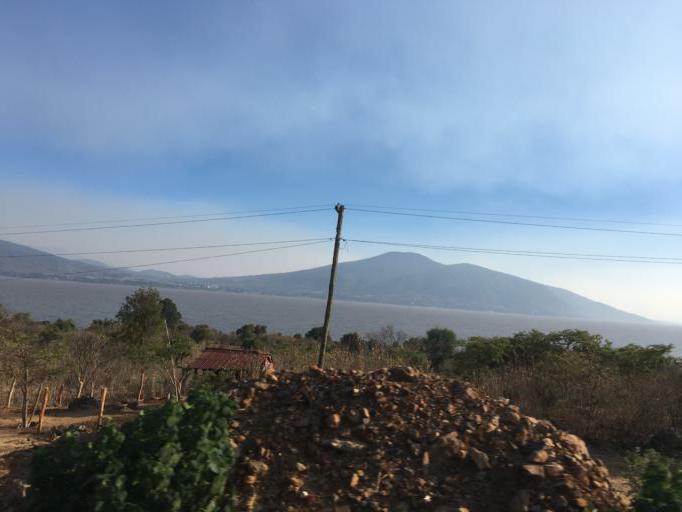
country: MX
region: Michoacan
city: Santa Fe de la Laguna
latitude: 19.6715
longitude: -101.5724
